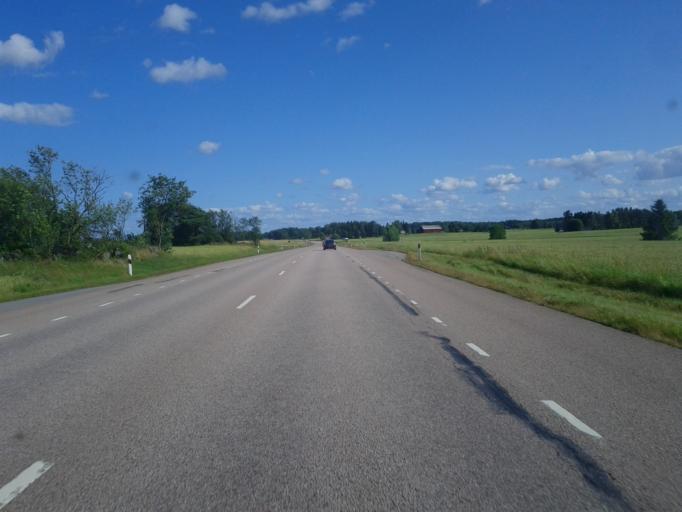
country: SE
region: Uppsala
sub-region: Enkopings Kommun
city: Enkoping
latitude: 59.6858
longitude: 17.0372
